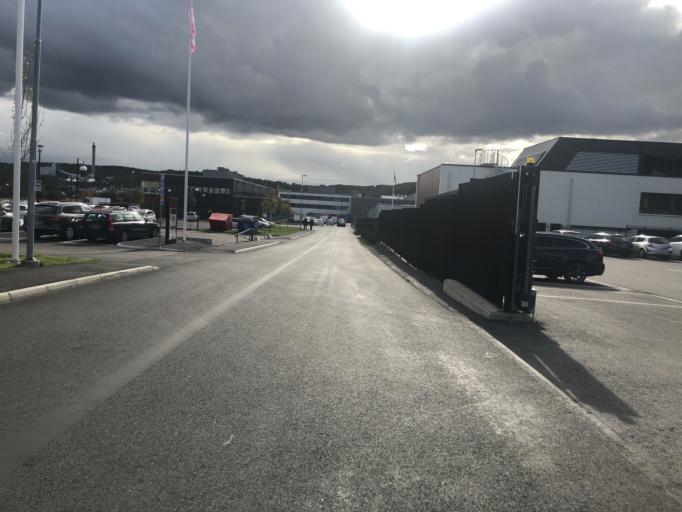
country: SE
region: Vaestra Goetaland
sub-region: Molndal
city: Moelndal
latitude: 57.6486
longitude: 11.9818
